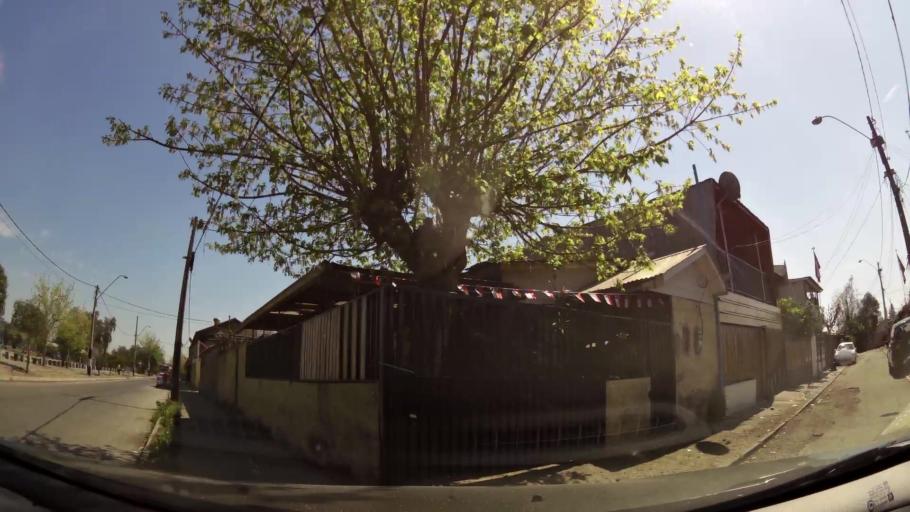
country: CL
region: Santiago Metropolitan
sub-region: Provincia de Santiago
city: La Pintana
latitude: -33.5910
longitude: -70.6237
